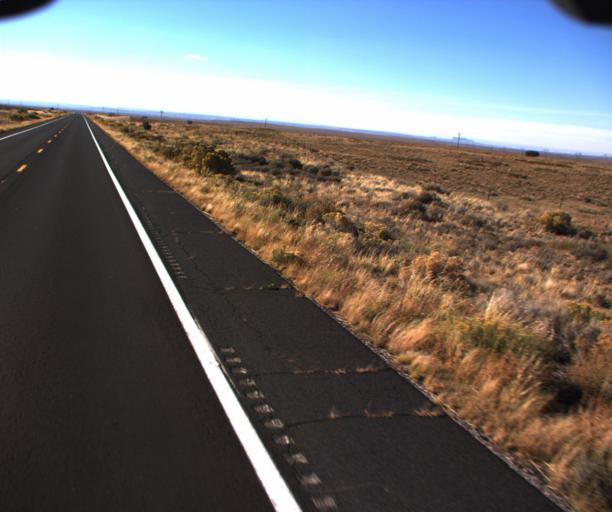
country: US
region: Arizona
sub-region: Coconino County
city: Kaibito
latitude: 36.6157
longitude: -110.9375
